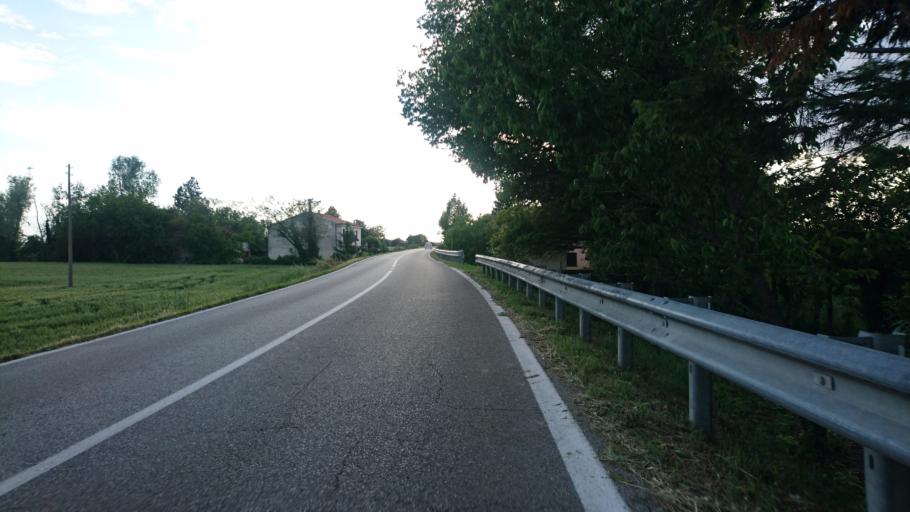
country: IT
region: Veneto
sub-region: Provincia di Rovigo
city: Ceneselli
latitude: 45.0215
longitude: 11.3518
